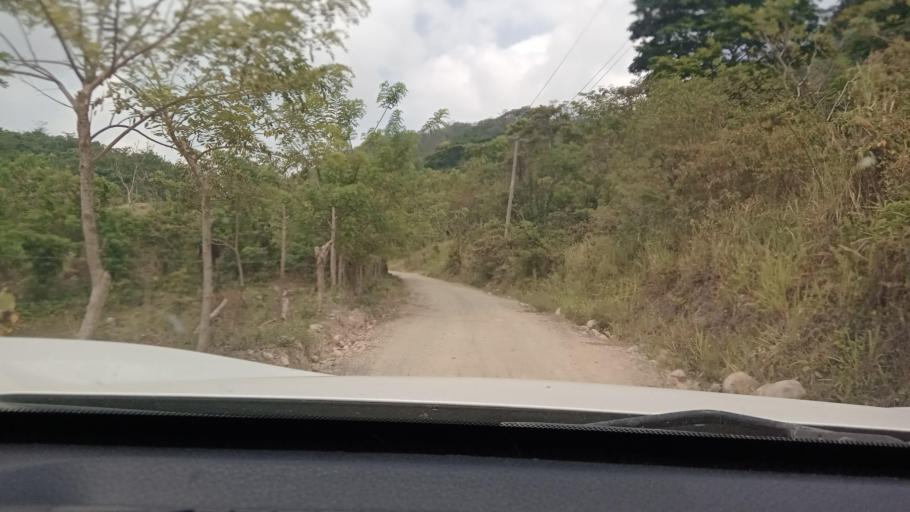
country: MX
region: Tabasco
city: Chontalpa
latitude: 17.4943
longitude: -93.6585
